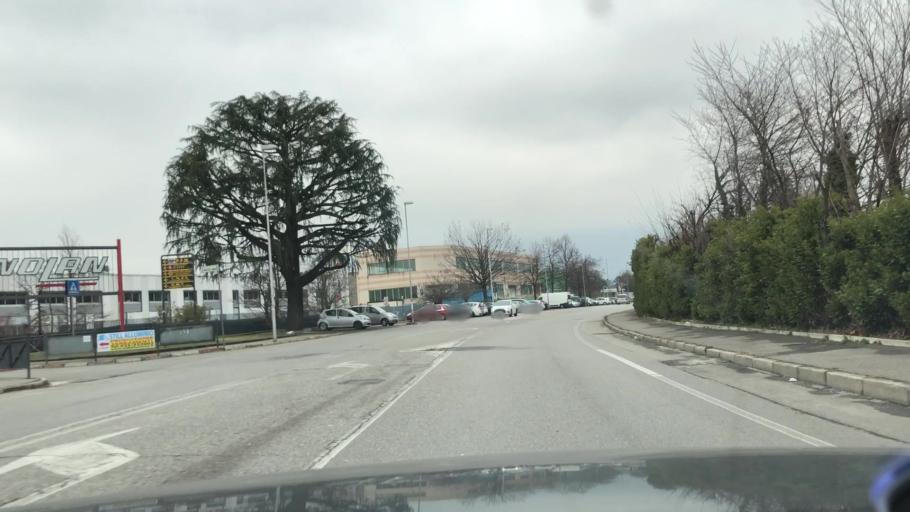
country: IT
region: Lombardy
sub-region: Provincia di Bergamo
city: Brembate di Sopra
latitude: 45.7096
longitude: 9.5827
